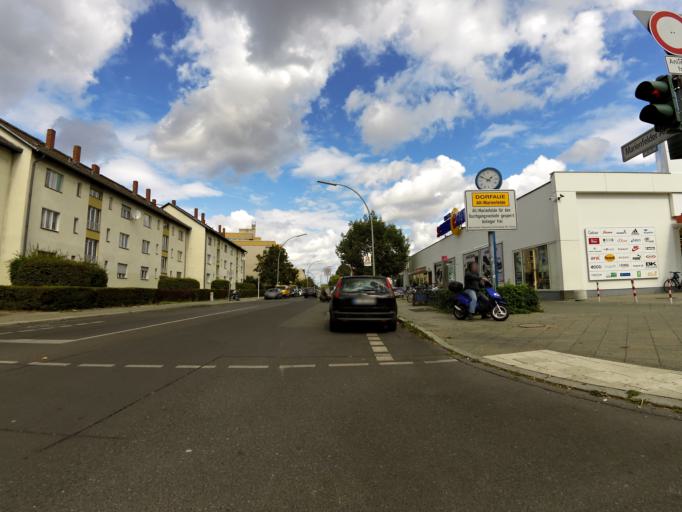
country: DE
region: Berlin
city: Marienfelde
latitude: 52.4124
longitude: 13.3624
